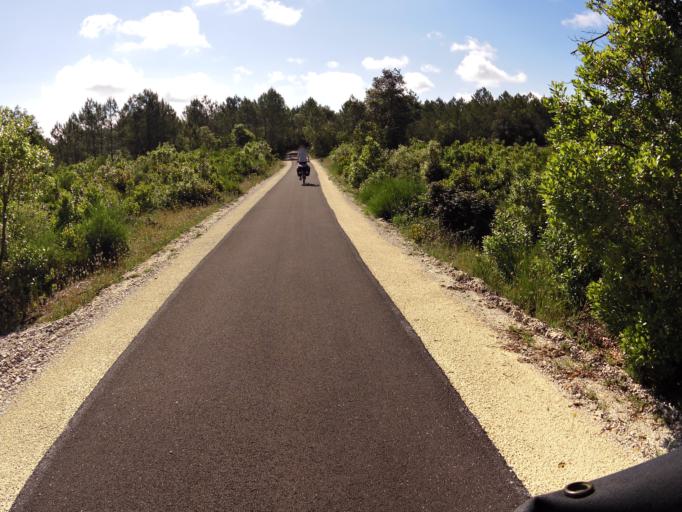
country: FR
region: Aquitaine
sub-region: Departement de la Gironde
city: Lacanau
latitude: 45.0324
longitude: -1.1779
